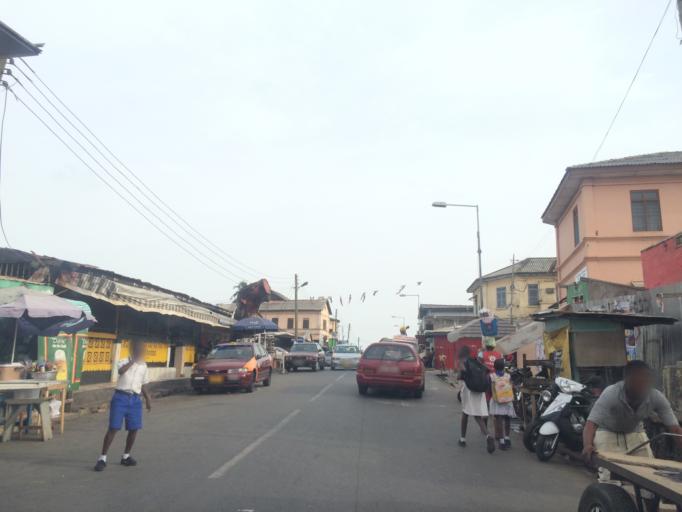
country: GH
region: Greater Accra
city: Accra
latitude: 5.5435
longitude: -0.2134
